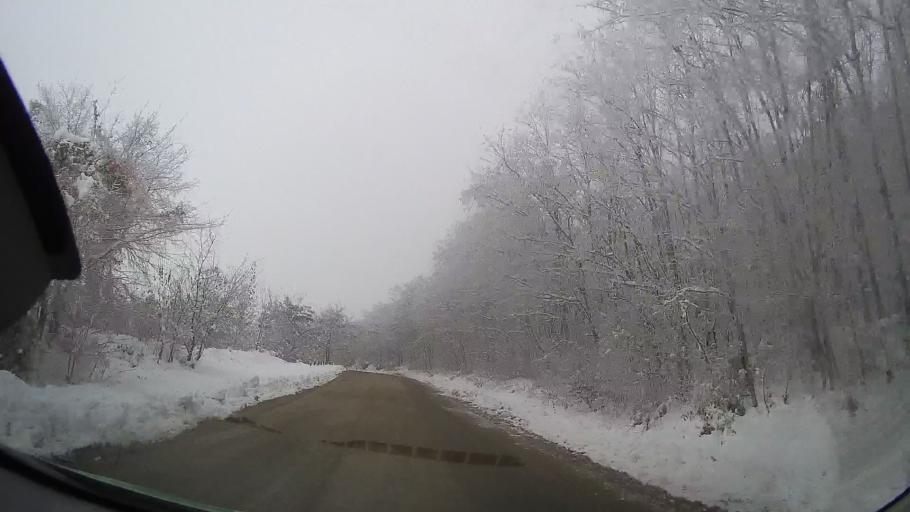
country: RO
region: Iasi
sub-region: Comuna Tansa
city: Suhulet
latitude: 46.8981
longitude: 27.2424
